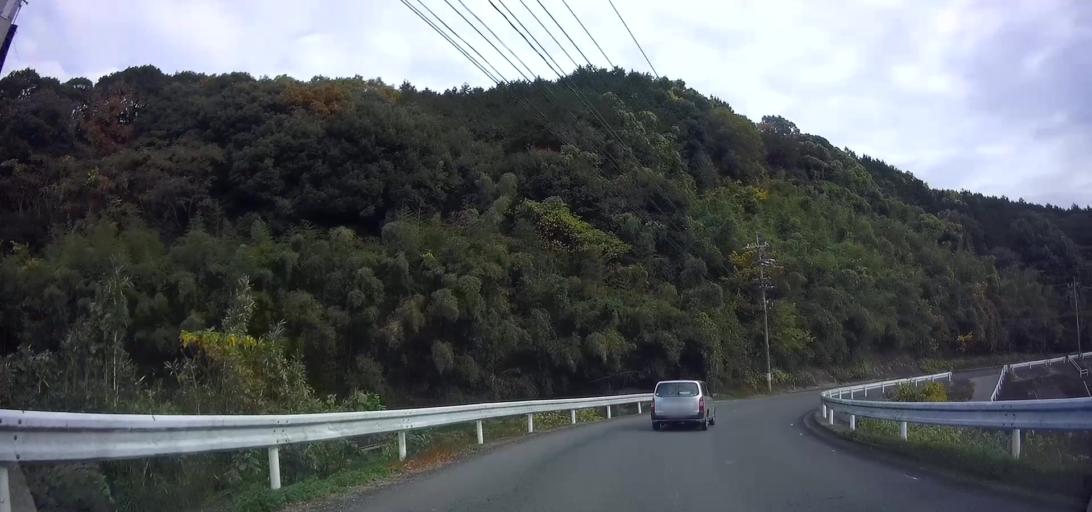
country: JP
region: Nagasaki
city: Shimabara
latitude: 32.6877
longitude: 130.2842
